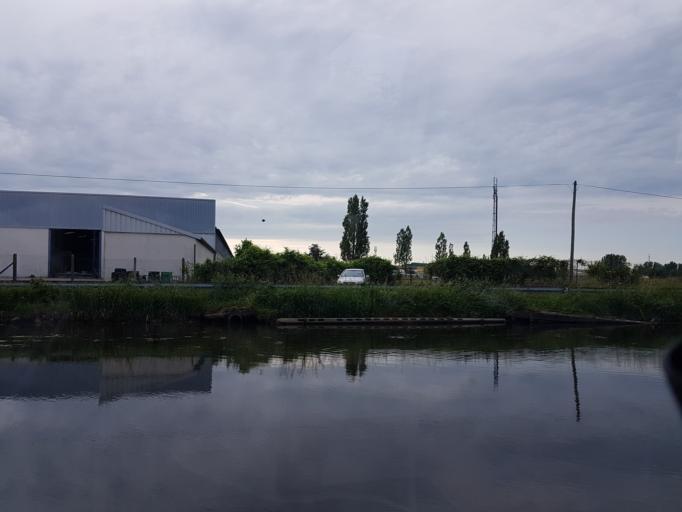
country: FR
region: Bourgogne
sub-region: Departement de l'Yonne
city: Auxerre
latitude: 47.8139
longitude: 3.5797
